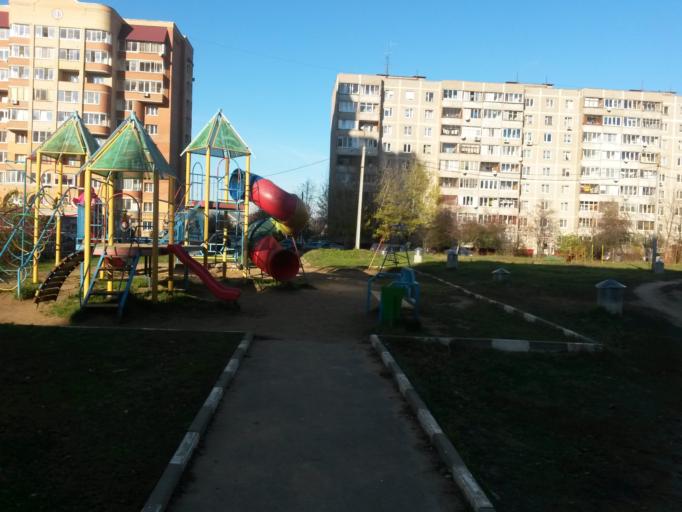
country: RU
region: Moskovskaya
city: Domodedovo
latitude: 55.4253
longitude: 37.7615
